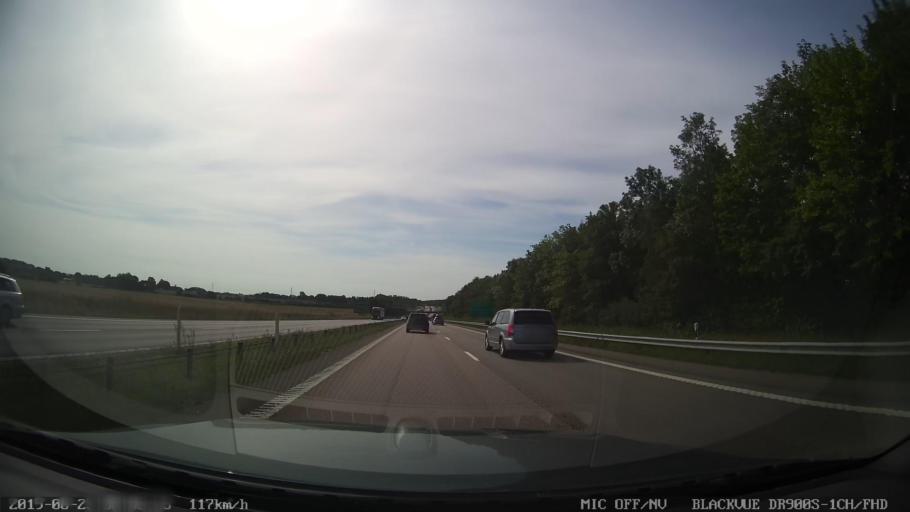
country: SE
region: Skane
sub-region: Helsingborg
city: Barslov
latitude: 56.0260
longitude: 12.7862
